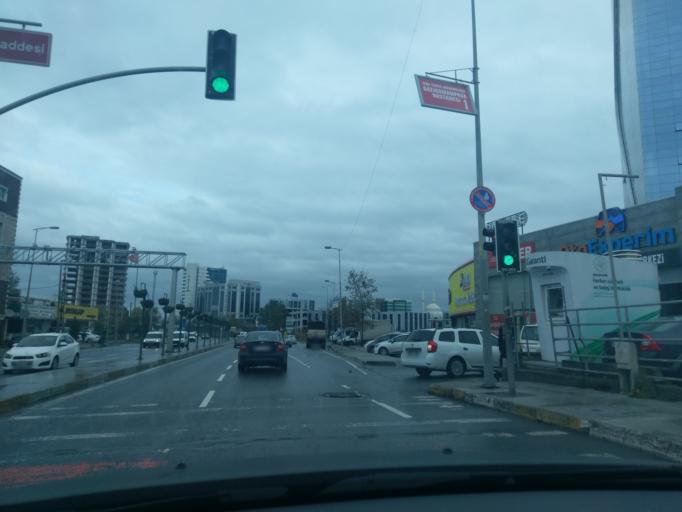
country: TR
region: Istanbul
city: Mahmutbey
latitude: 41.0620
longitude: 28.8326
